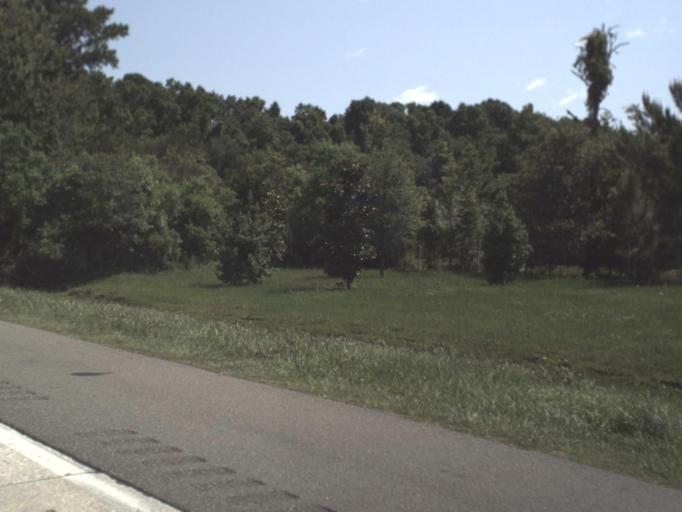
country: US
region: Florida
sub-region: Duval County
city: Jacksonville
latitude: 30.4160
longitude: -81.6568
